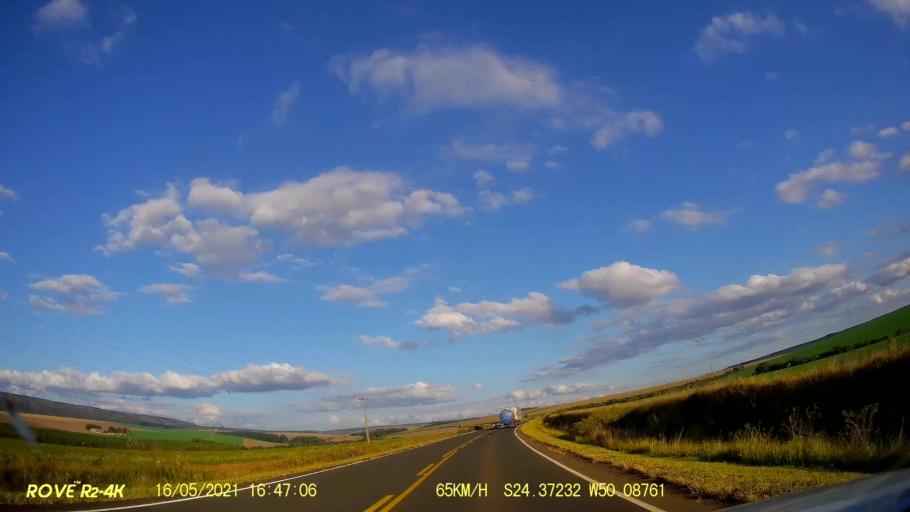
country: BR
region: Parana
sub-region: Pirai Do Sul
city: Pirai do Sul
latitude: -24.3725
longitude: -50.0874
